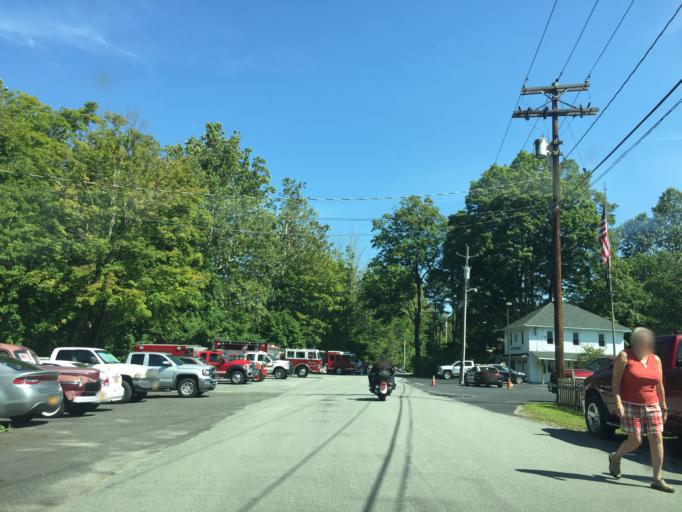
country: US
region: New York
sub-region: Sullivan County
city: Livingston Manor
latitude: 41.7655
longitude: -75.0306
